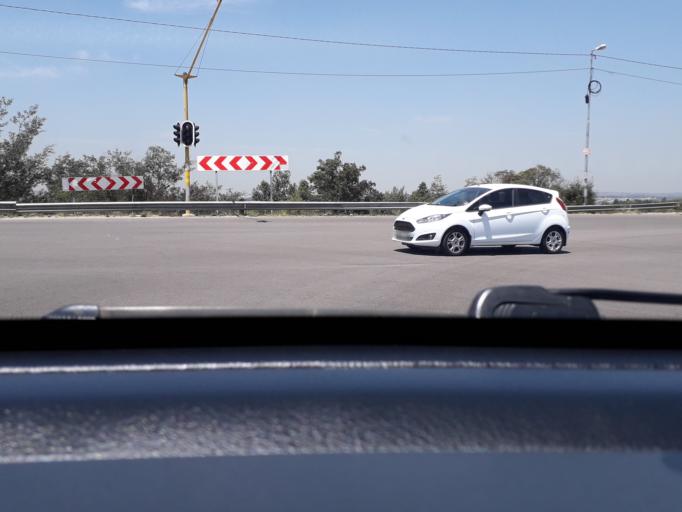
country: ZA
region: Gauteng
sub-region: City of Johannesburg Metropolitan Municipality
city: Modderfontein
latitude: -26.0659
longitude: 28.0923
